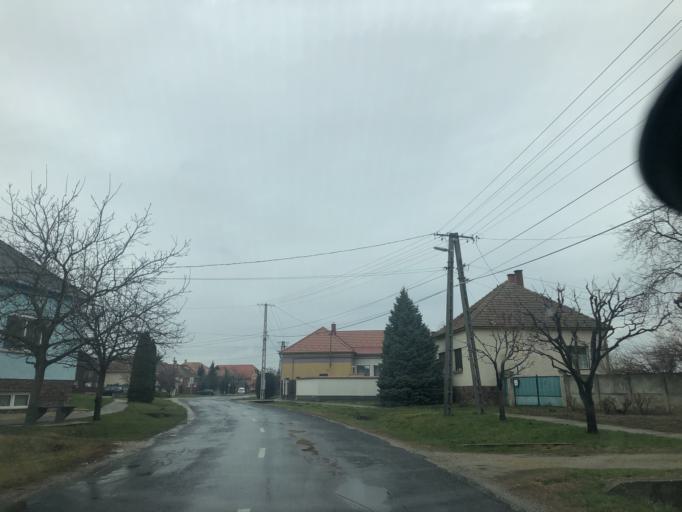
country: HU
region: Gyor-Moson-Sopron
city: Fertoszentmiklos
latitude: 47.6052
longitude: 16.9477
